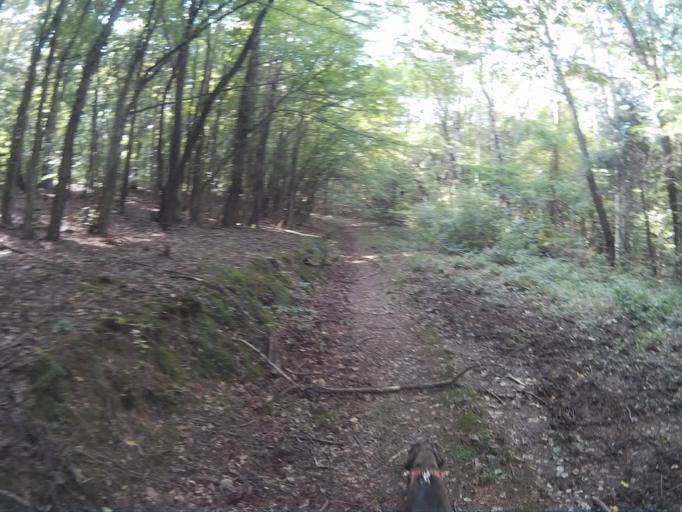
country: AT
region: Burgenland
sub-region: Politischer Bezirk Oberpullendorf
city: Mannersdorf an der Rabnitz
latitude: 47.4057
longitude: 16.5092
